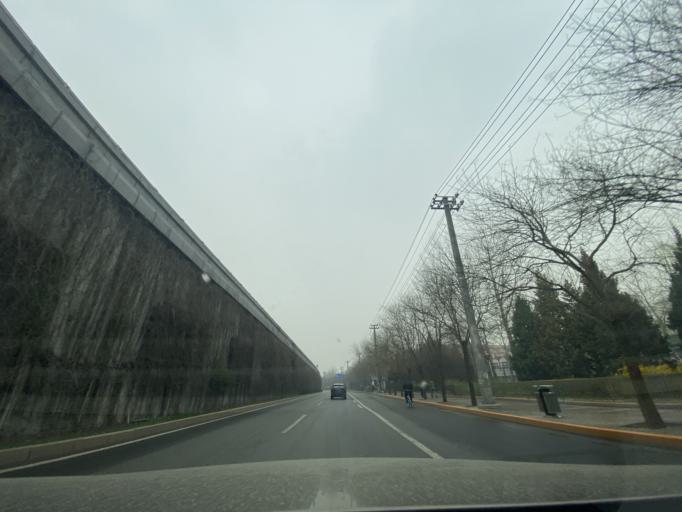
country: CN
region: Beijing
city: Sijiqing
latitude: 39.9676
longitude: 116.2686
